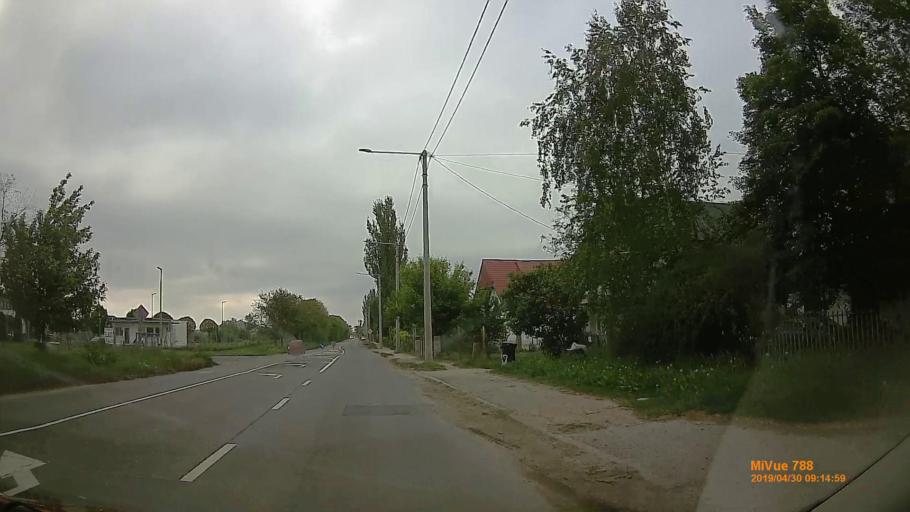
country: HU
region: Pest
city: Vac
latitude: 47.7611
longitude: 19.1472
